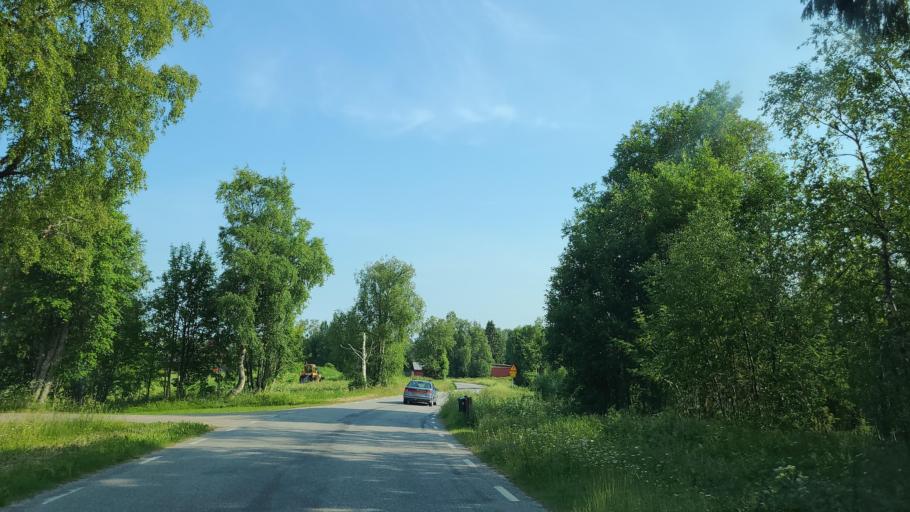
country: SE
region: Vaesterbotten
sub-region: Skelleftea Kommun
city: Burea
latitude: 64.3495
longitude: 21.3366
